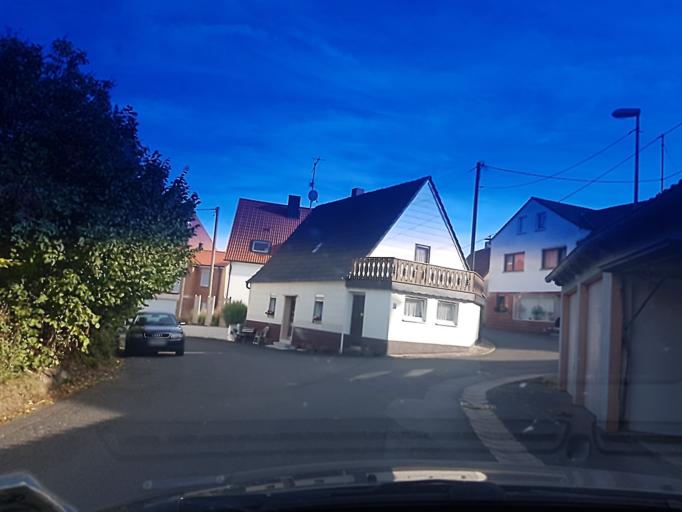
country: DE
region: Bavaria
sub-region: Regierungsbezirk Mittelfranken
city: Burghaslach
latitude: 49.7733
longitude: 10.5609
